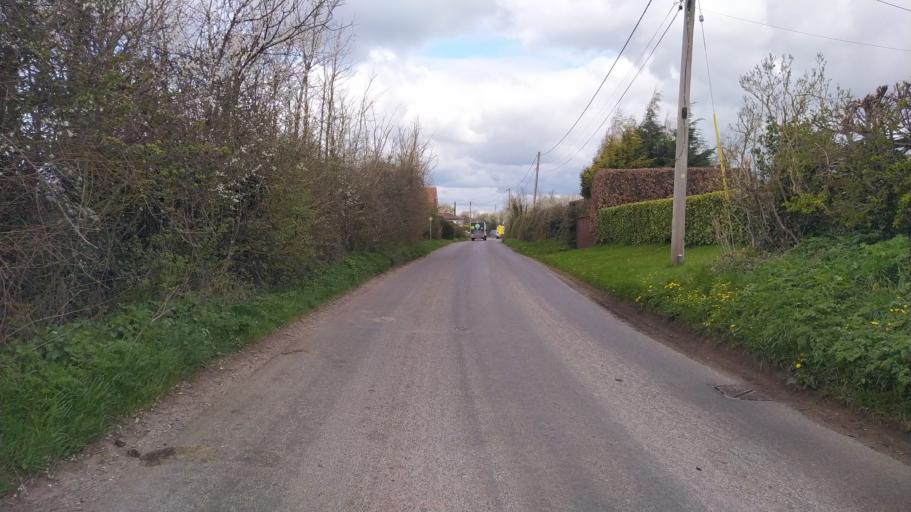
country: GB
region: England
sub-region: Wiltshire
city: North Bradley
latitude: 51.2938
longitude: -2.1690
